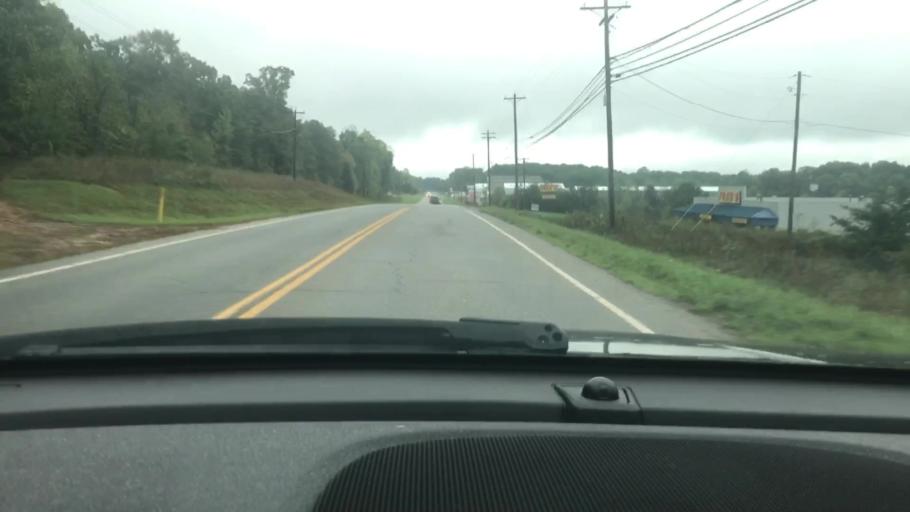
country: US
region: Tennessee
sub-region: Dickson County
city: White Bluff
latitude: 36.1048
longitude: -87.1990
